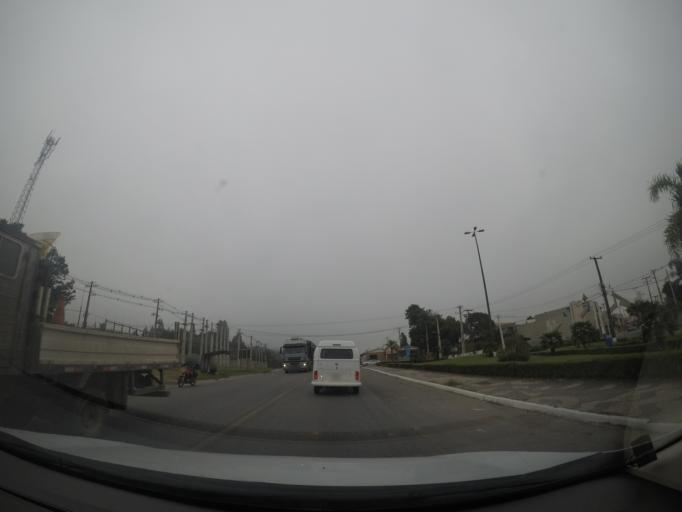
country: BR
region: Parana
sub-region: Almirante Tamandare
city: Almirante Tamandare
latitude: -25.3160
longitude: -49.3019
